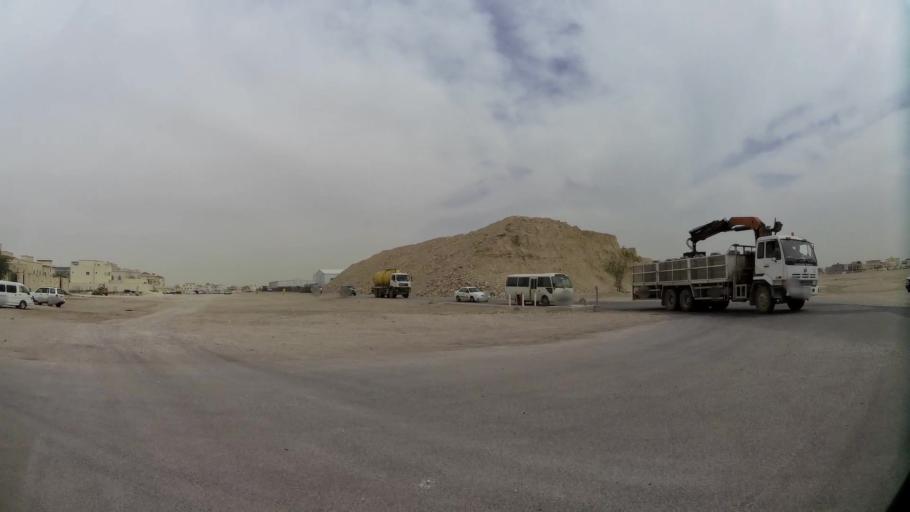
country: QA
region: Baladiyat ar Rayyan
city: Ar Rayyan
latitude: 25.2049
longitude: 51.4584
